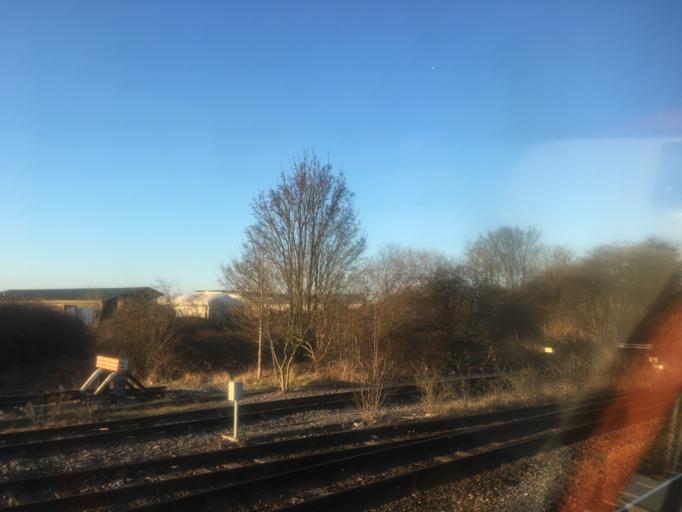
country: GB
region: England
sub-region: Derbyshire
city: Long Eaton
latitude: 52.8897
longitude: -1.2597
